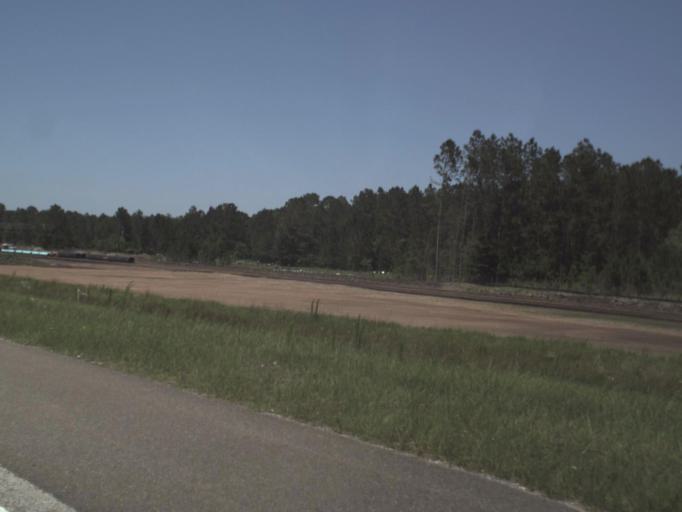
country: US
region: Florida
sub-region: Clay County
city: Bellair-Meadowbrook Terrace
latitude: 30.2423
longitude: -81.8439
